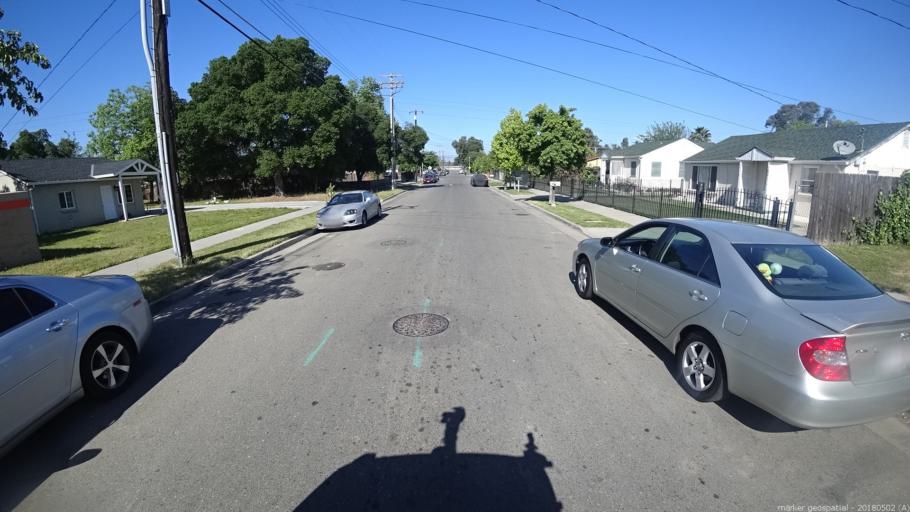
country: US
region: California
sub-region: Sacramento County
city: Arden-Arcade
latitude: 38.6129
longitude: -121.4288
